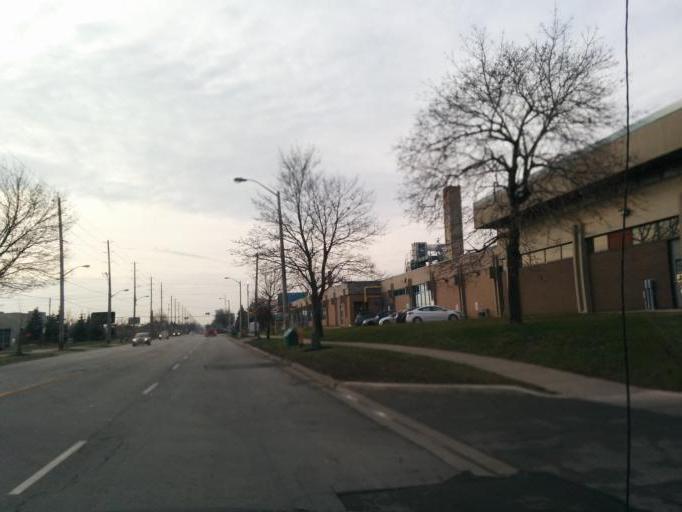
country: CA
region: Ontario
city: Etobicoke
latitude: 43.6156
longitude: -79.5271
